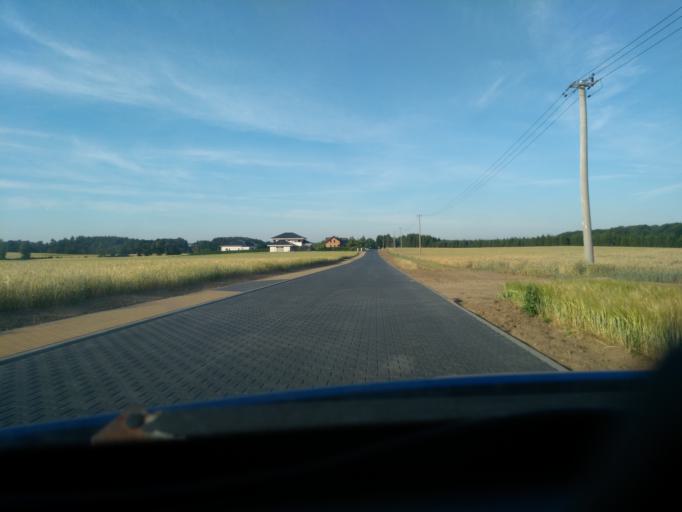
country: PL
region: Pomeranian Voivodeship
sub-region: Powiat kartuski
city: Przodkowo
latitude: 54.3886
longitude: 18.3207
